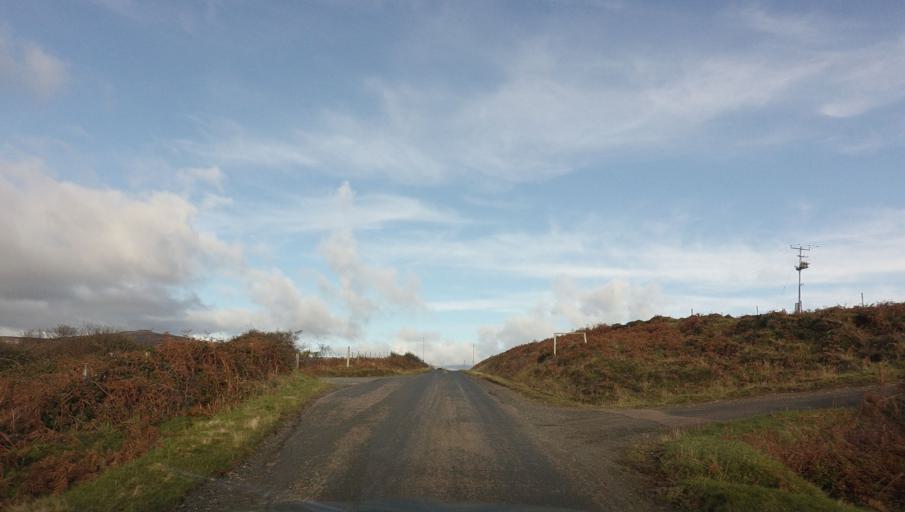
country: GB
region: Scotland
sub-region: Argyll and Bute
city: Isle Of Mull
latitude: 56.3263
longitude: -6.2034
